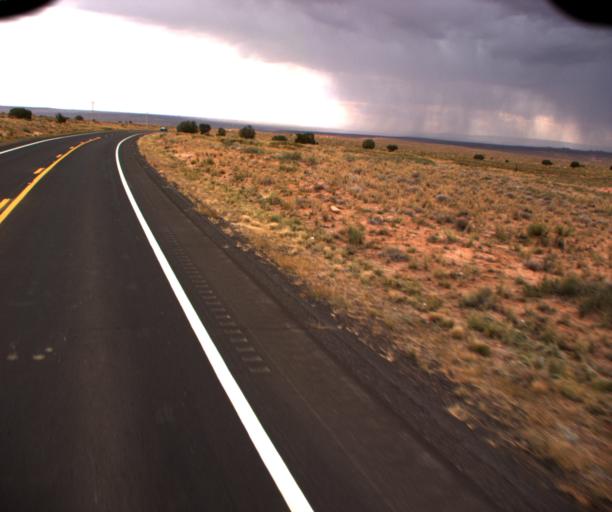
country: US
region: Arizona
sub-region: Coconino County
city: Tuba City
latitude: 36.2385
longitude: -111.0258
